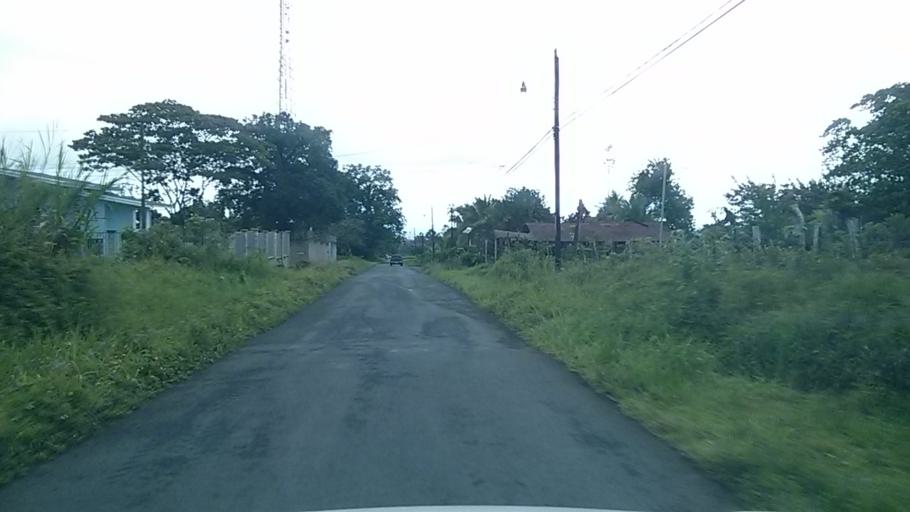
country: CR
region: Limon
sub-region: Canton de Pococi
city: Guapiles
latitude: 10.1826
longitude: -83.7832
